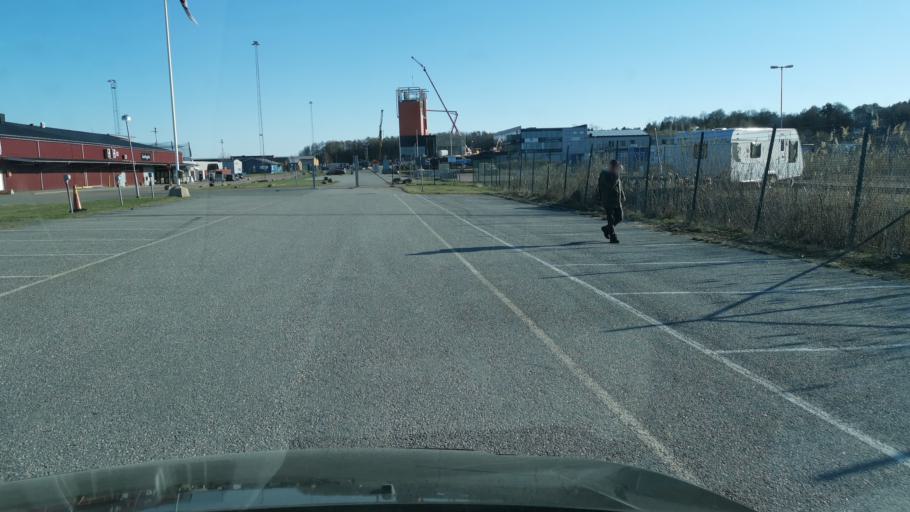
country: SE
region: Vaestra Goetaland
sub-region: Goteborg
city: Majorna
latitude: 57.7789
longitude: 11.8641
